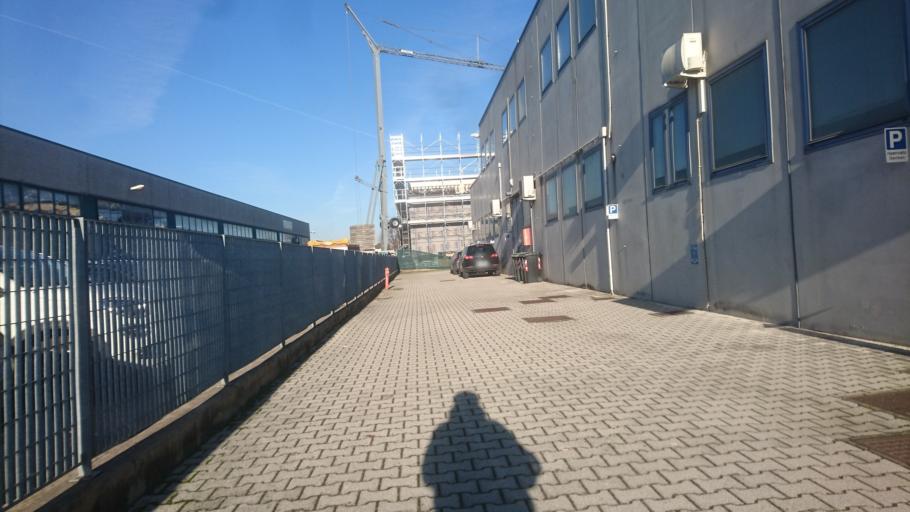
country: IT
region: Veneto
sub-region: Provincia di Padova
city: Limena
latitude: 45.4638
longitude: 11.8454
